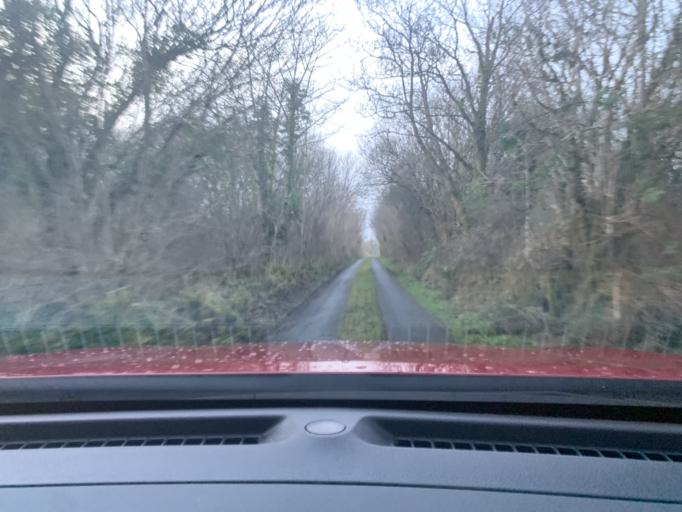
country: IE
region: Connaught
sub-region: Sligo
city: Ballymote
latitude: 53.9905
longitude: -8.4496
